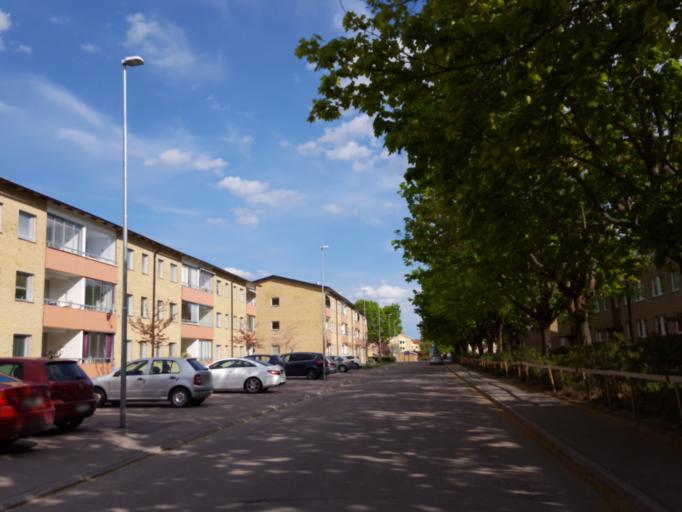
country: SE
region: Uppsala
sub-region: Uppsala Kommun
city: Uppsala
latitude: 59.8700
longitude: 17.6589
